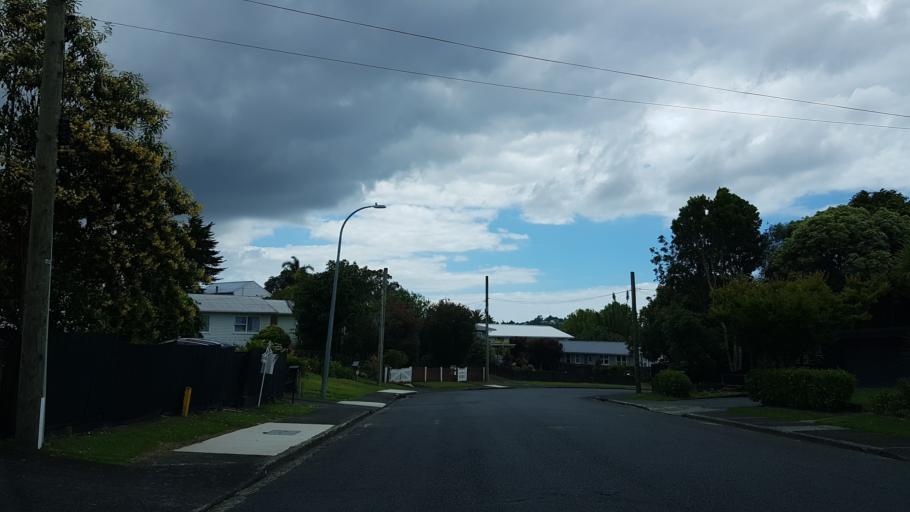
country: NZ
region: Auckland
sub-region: Auckland
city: North Shore
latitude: -36.7961
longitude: 174.6929
